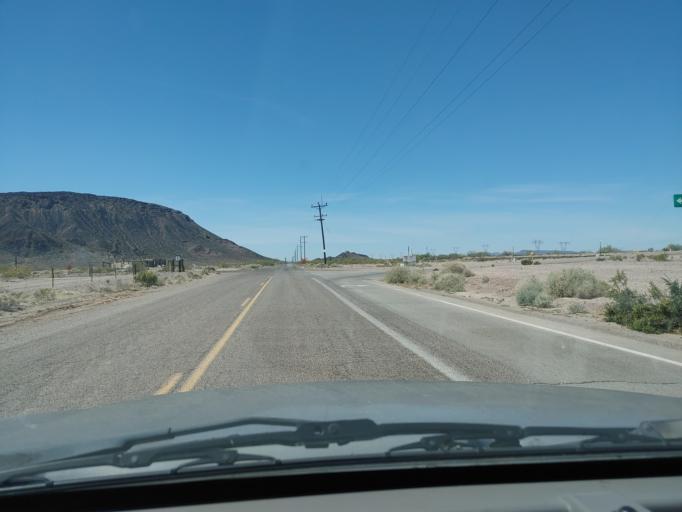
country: US
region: Arizona
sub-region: Maricopa County
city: Gila Bend
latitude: 33.0208
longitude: -113.3396
